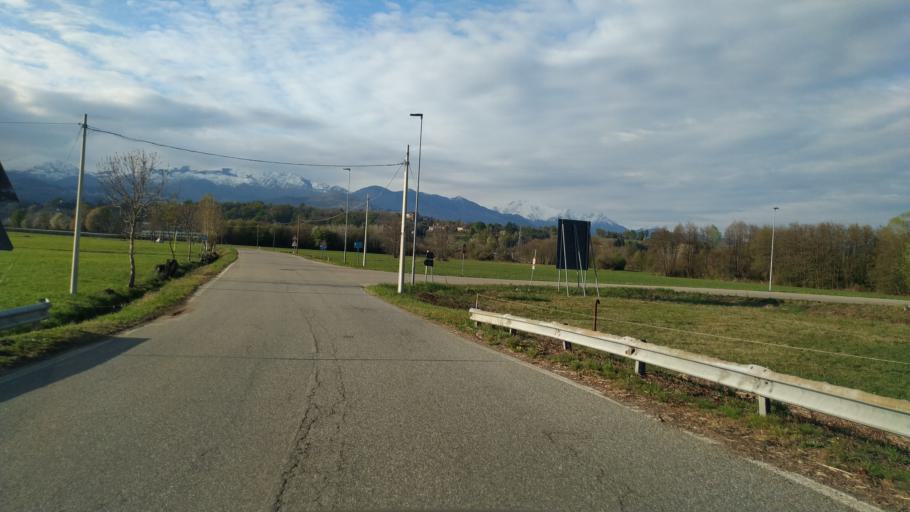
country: IT
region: Piedmont
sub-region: Provincia di Biella
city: Cerreto Castello
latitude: 45.5546
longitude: 8.1583
